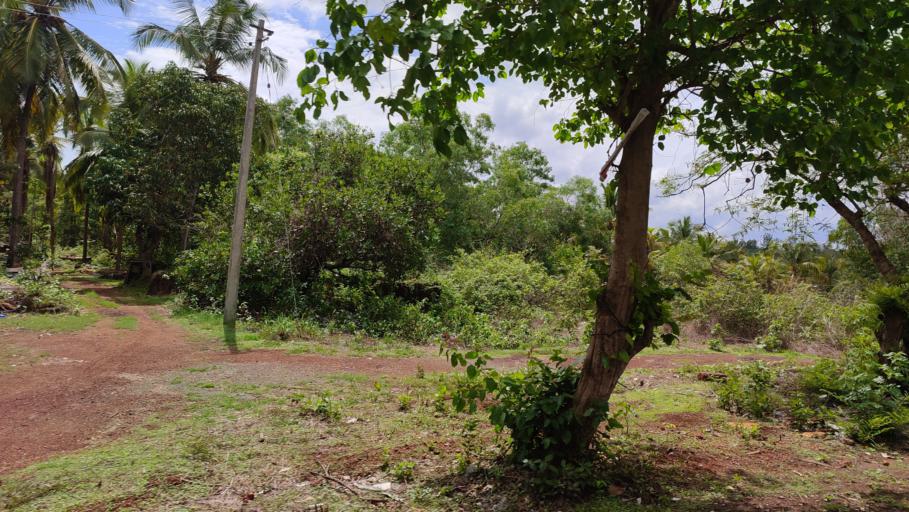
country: IN
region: Kerala
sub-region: Kasaragod District
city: Kannangad
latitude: 12.3889
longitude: 75.1019
